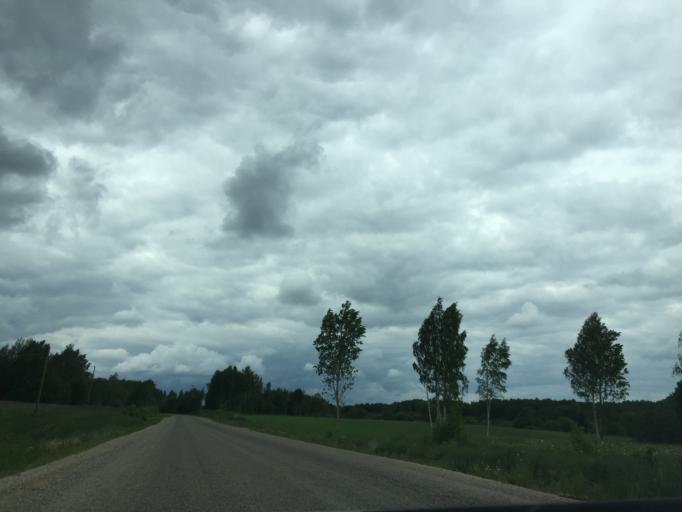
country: LV
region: Dagda
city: Dagda
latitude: 56.0653
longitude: 27.5613
